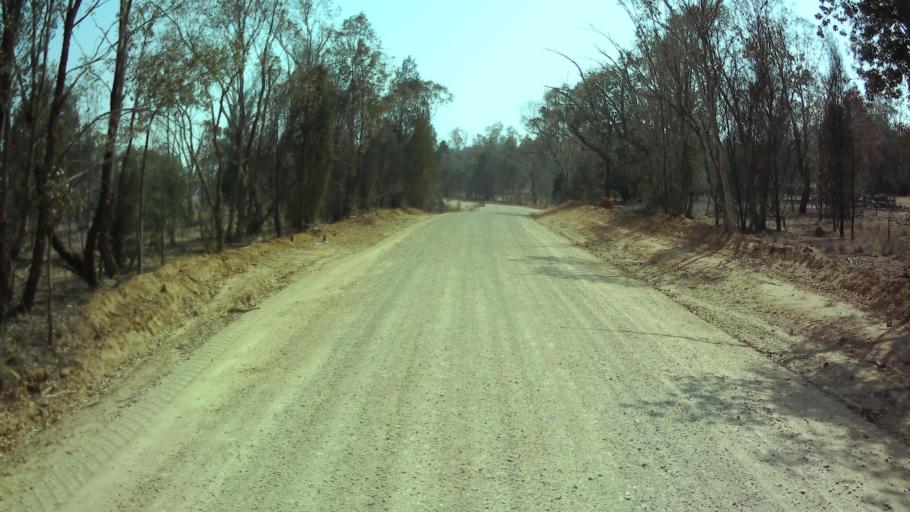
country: AU
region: New South Wales
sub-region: Weddin
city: Grenfell
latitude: -33.6627
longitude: 148.2746
